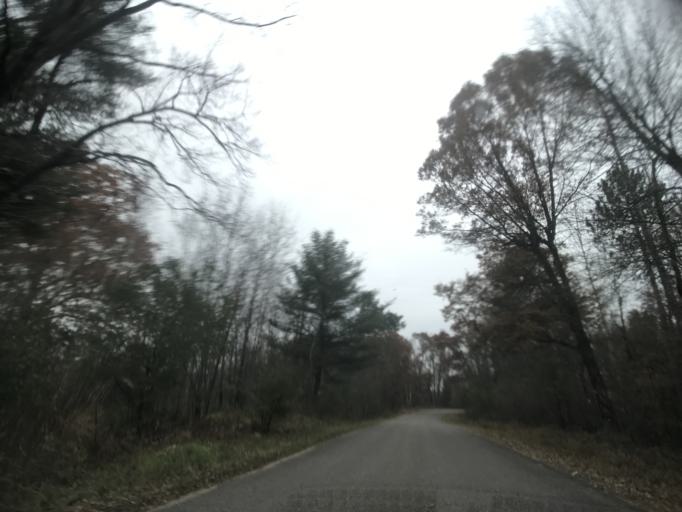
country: US
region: Michigan
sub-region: Dickinson County
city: Kingsford
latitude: 45.3831
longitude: -88.3214
